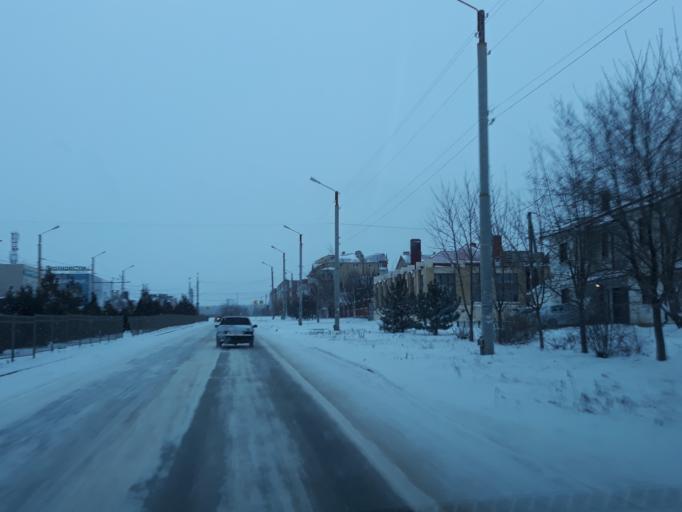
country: RU
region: Rostov
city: Taganrog
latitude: 47.2750
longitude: 38.9173
